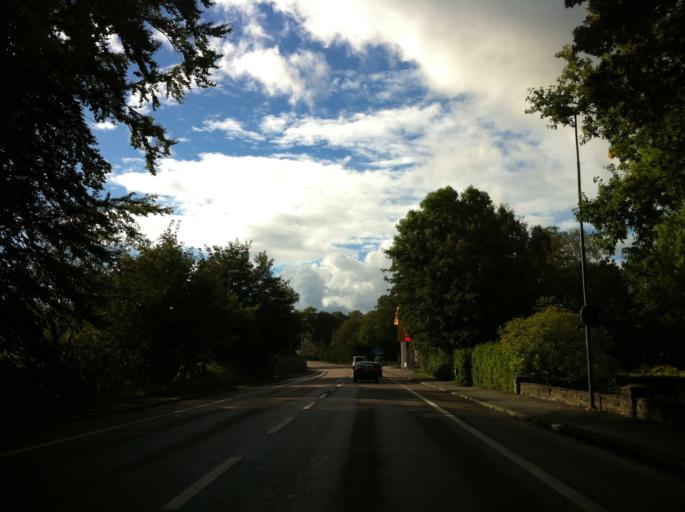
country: SE
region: Skane
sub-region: Hassleholms Kommun
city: Tormestorp
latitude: 56.1628
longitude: 13.5929
